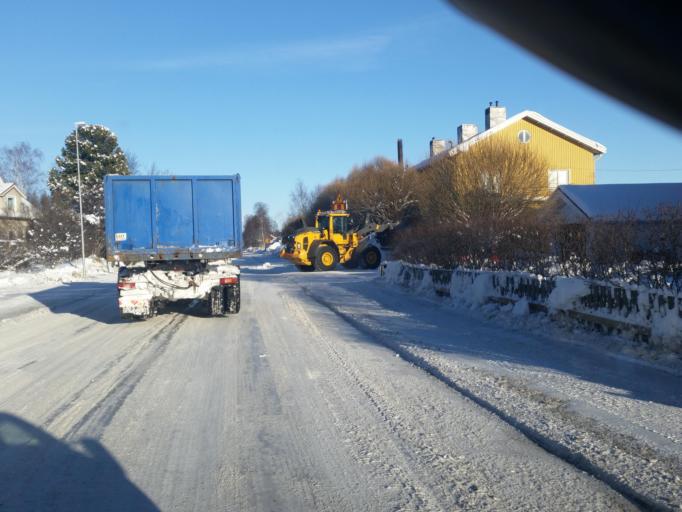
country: SE
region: Norrbotten
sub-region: Pitea Kommun
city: Hortlax
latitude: 65.2838
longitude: 21.4072
